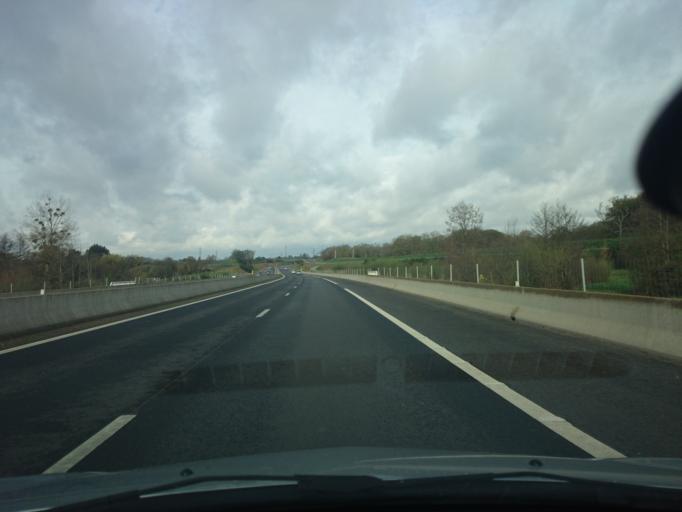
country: FR
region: Brittany
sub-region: Departement d'Ille-et-Vilaine
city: Vezin-le-Coquet
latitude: 48.1259
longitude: -1.7262
